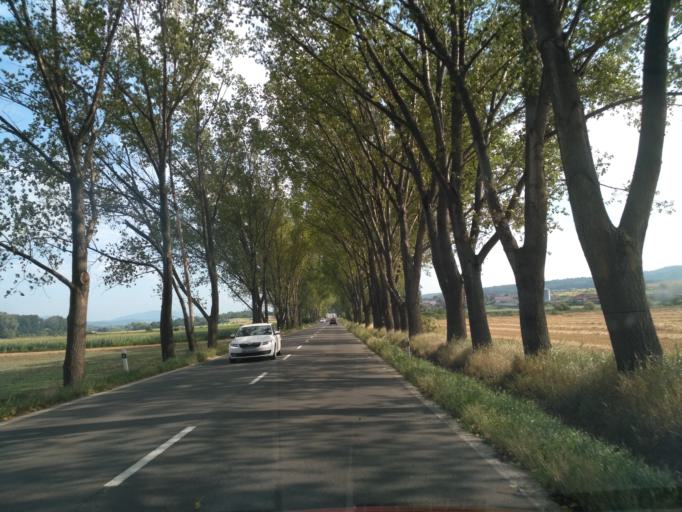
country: SK
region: Kosicky
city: Kosice
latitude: 48.8122
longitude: 21.3004
